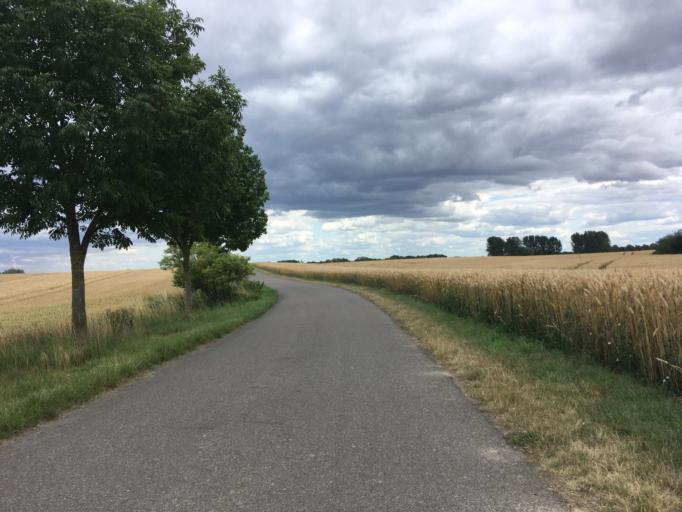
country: DE
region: Brandenburg
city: Gramzow
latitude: 53.2580
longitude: 13.9819
